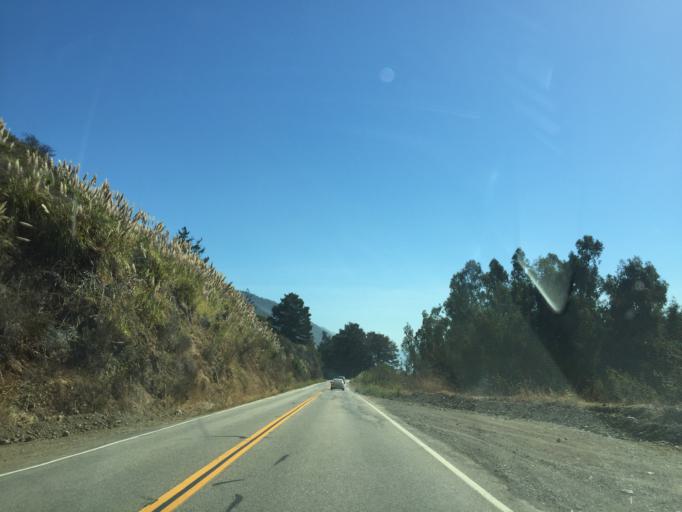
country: US
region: California
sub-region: Monterey County
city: Greenfield
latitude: 35.9942
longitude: -121.4972
